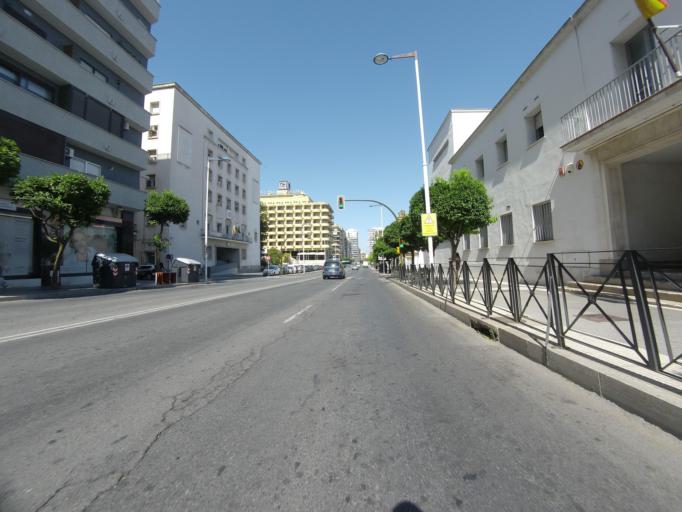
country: ES
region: Andalusia
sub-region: Provincia de Huelva
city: Huelva
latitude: 37.2546
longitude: -6.9422
